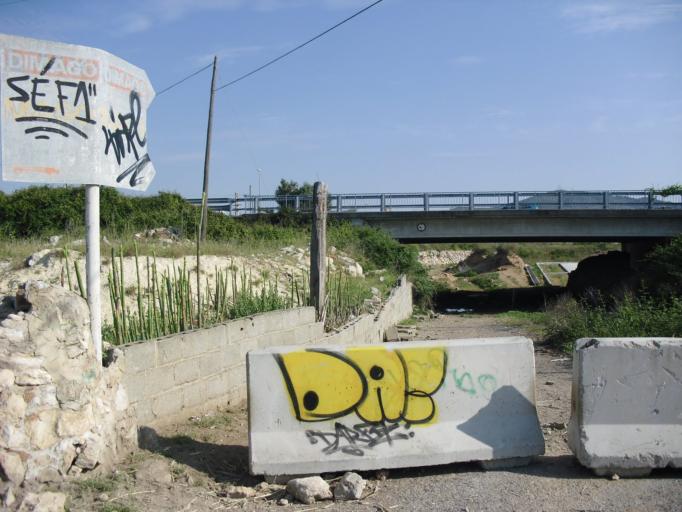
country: ES
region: Catalonia
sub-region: Provincia de Barcelona
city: Vilanova i la Geltru
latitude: 41.2363
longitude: 1.7314
